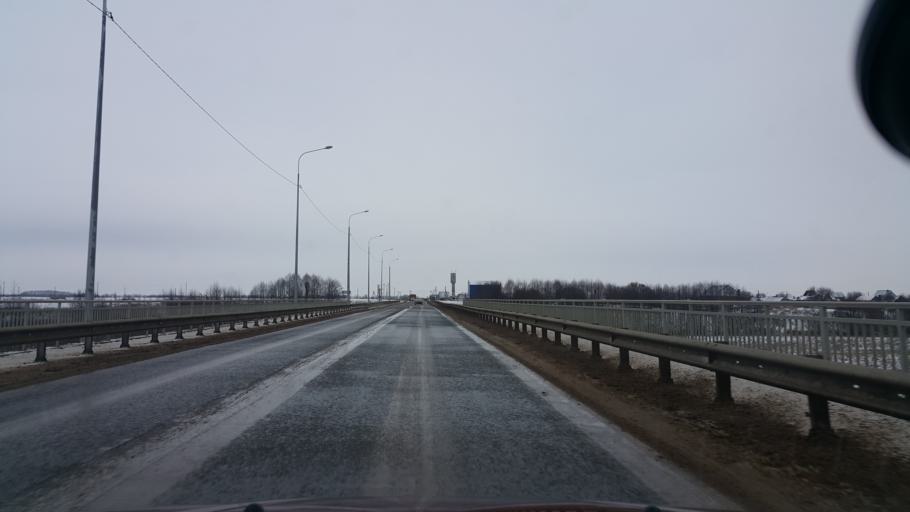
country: RU
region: Tambov
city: Bokino
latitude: 52.6162
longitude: 41.4661
